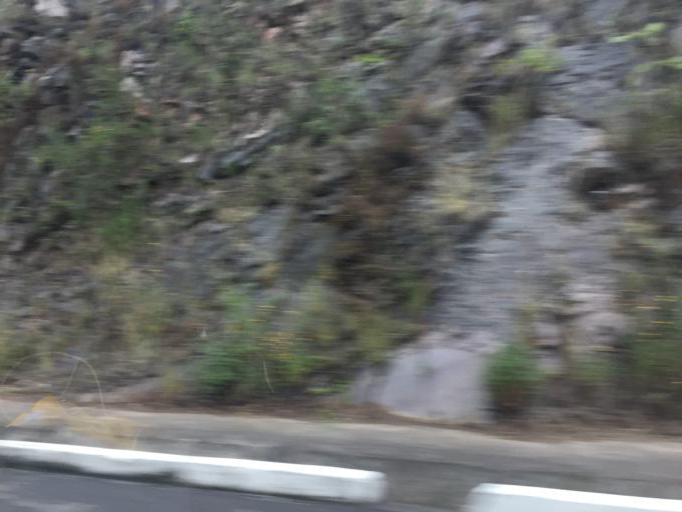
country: MX
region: Michoacan
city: Panindicuaro de la Reforma
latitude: 19.9737
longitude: -101.7361
